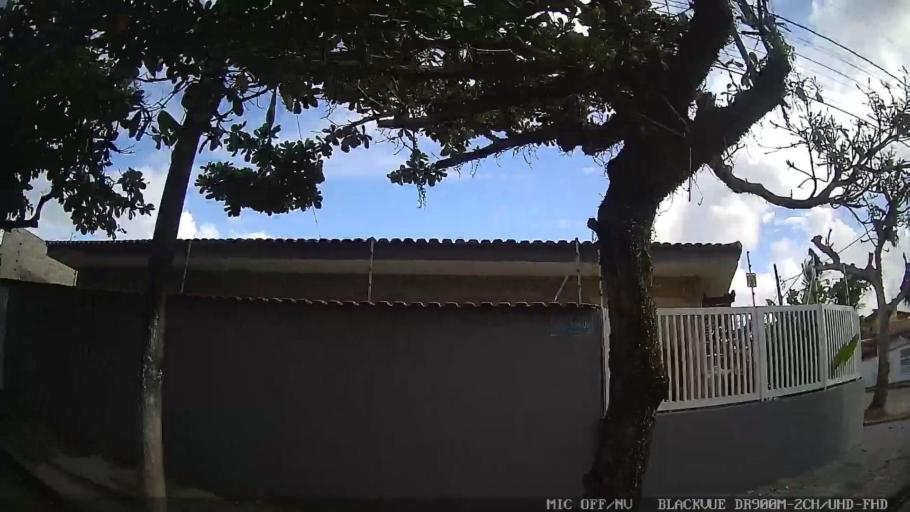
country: BR
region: Sao Paulo
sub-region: Itanhaem
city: Itanhaem
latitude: -24.2027
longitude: -46.8225
